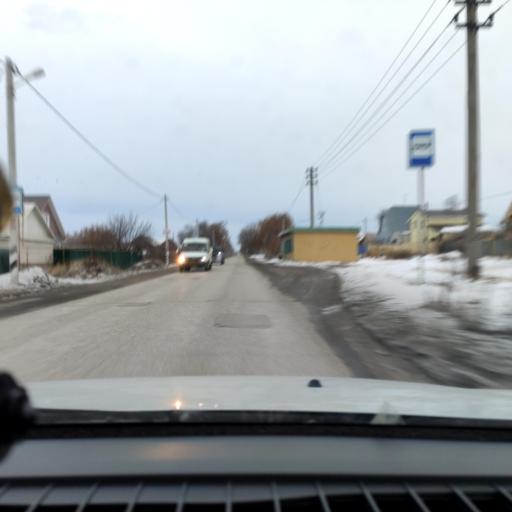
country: RU
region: Samara
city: Chapayevsk
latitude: 52.9984
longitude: 49.7170
